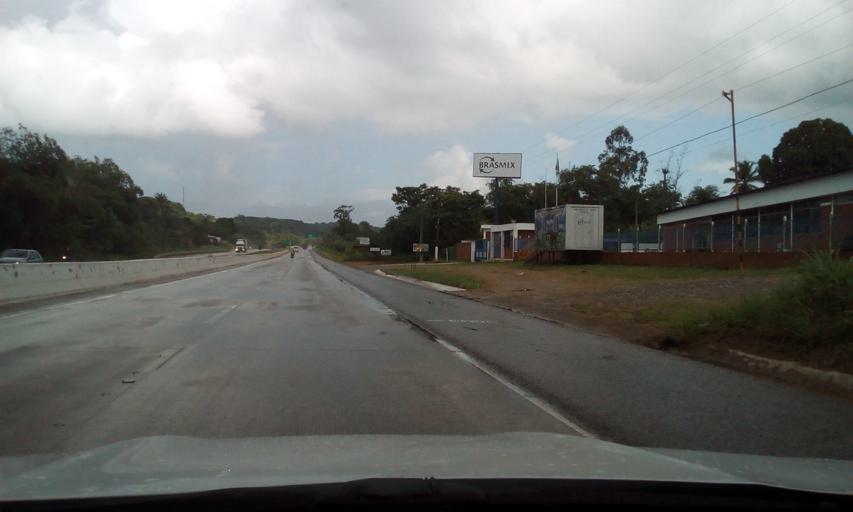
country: BR
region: Pernambuco
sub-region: Cabo De Santo Agostinho
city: Cabo
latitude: -8.3089
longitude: -35.0865
